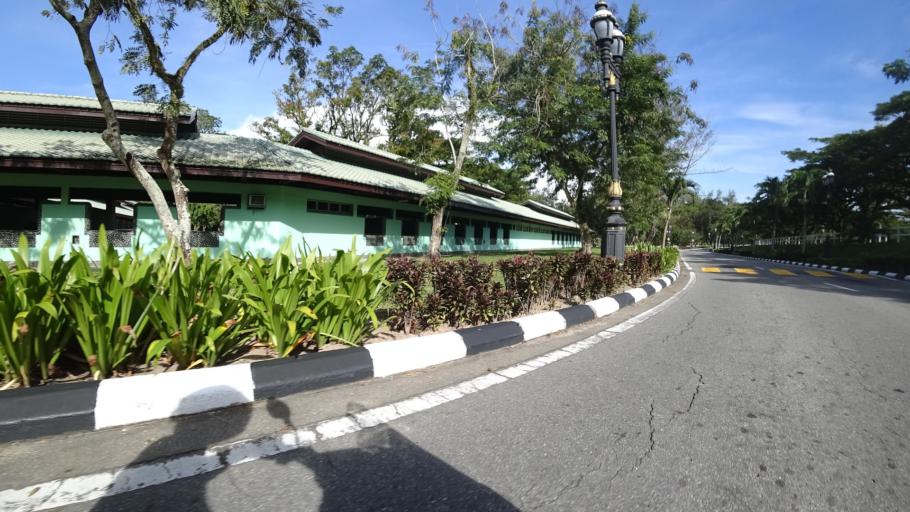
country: BN
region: Brunei and Muara
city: Bandar Seri Begawan
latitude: 4.9482
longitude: 114.8319
